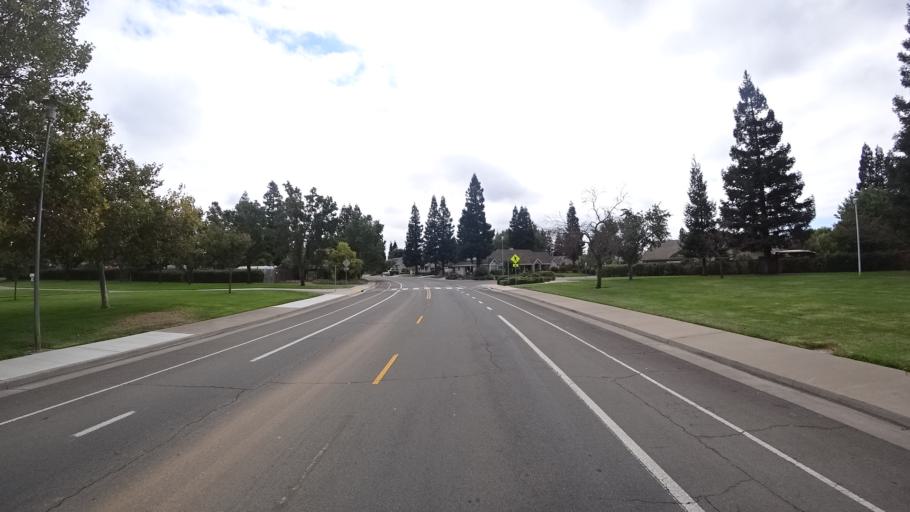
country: US
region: California
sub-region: Sacramento County
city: Laguna
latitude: 38.4202
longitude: -121.4381
